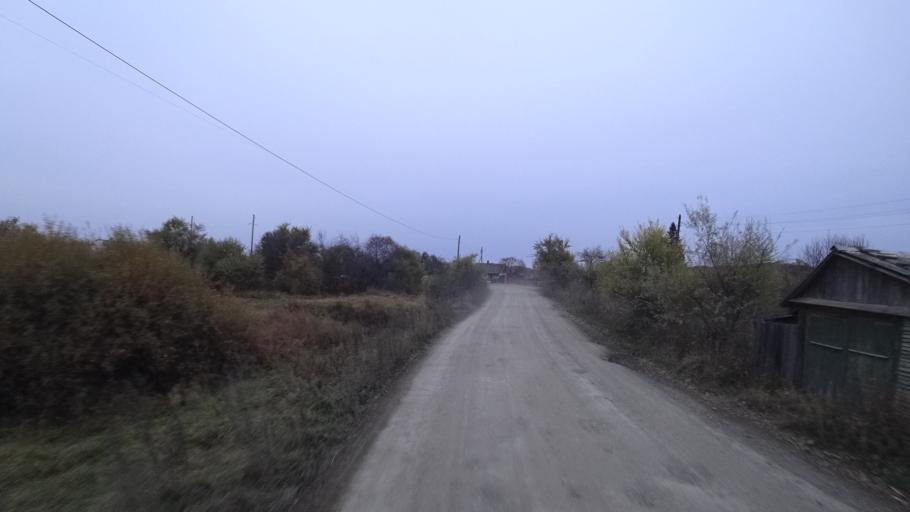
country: RU
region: Khabarovsk Krai
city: Amursk
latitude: 49.9026
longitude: 136.1432
